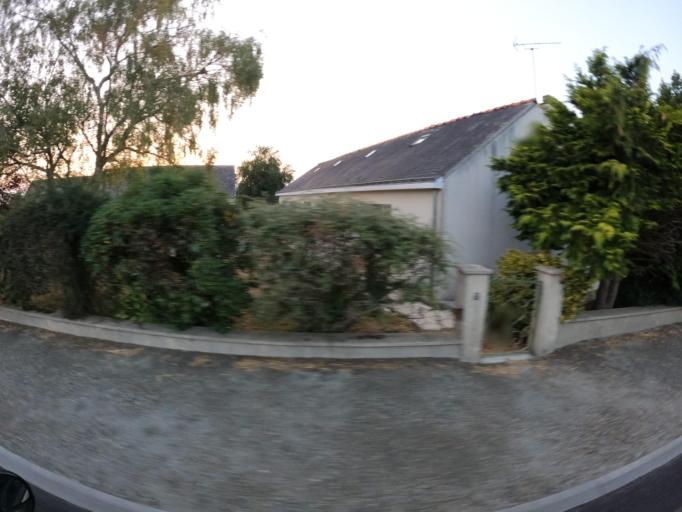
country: FR
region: Pays de la Loire
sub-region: Departement de Maine-et-Loire
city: Segre
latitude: 47.7352
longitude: -0.8345
